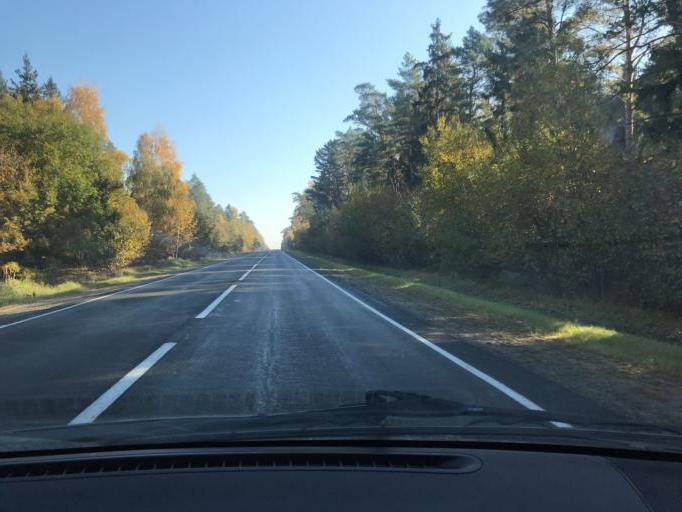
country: BY
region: Brest
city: Lyakhavichy
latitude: 52.9596
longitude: 26.3846
